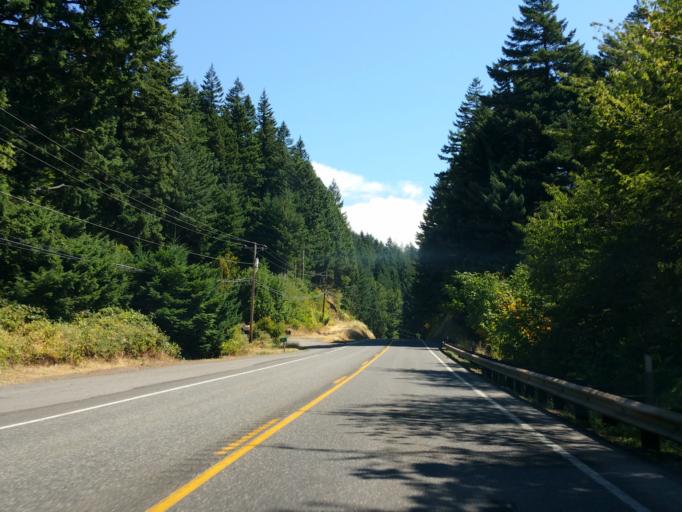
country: US
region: Washington
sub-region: Skamania County
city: Stevenson
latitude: 45.7058
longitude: -121.8515
